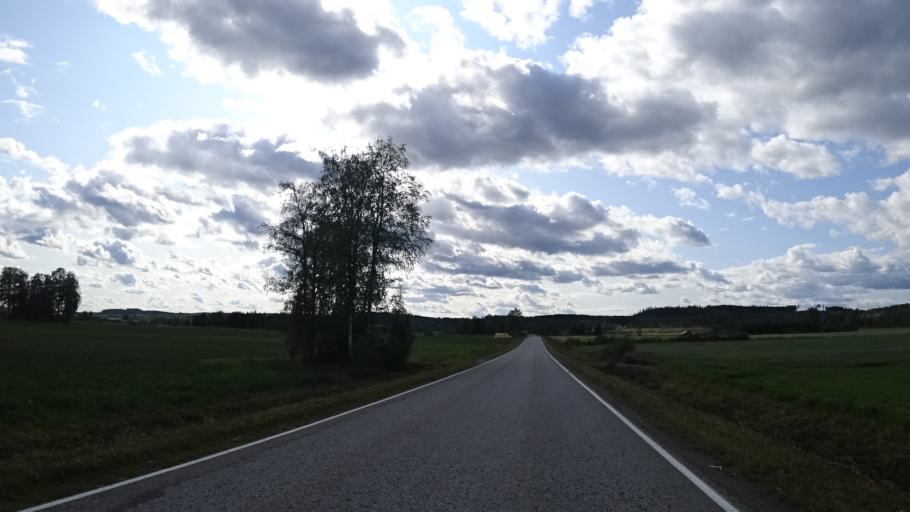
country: RU
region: Republic of Karelia
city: Vyartsilya
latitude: 62.2219
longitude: 30.6314
